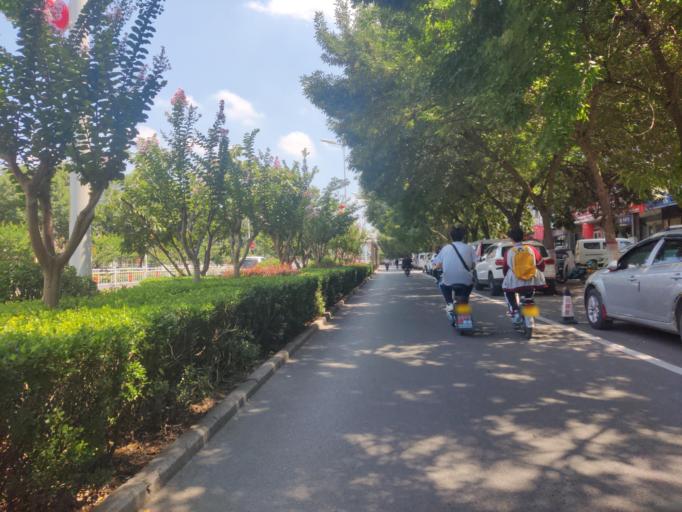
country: CN
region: Henan Sheng
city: Puyang
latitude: 35.7724
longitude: 115.0215
